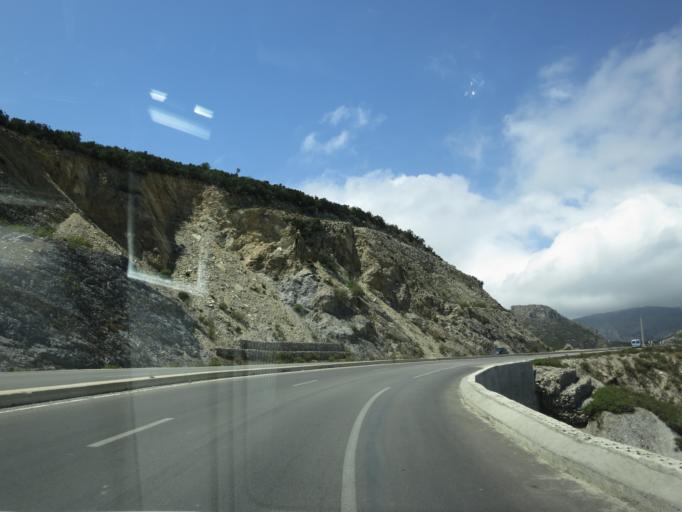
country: ES
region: Ceuta
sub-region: Ceuta
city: Ceuta
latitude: 35.8681
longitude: -5.3817
